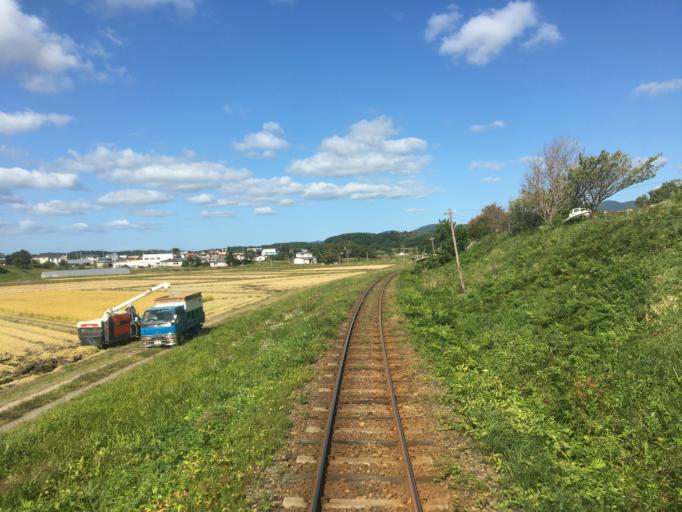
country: JP
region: Aomori
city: Goshogawara
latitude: 40.9487
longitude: 140.4386
